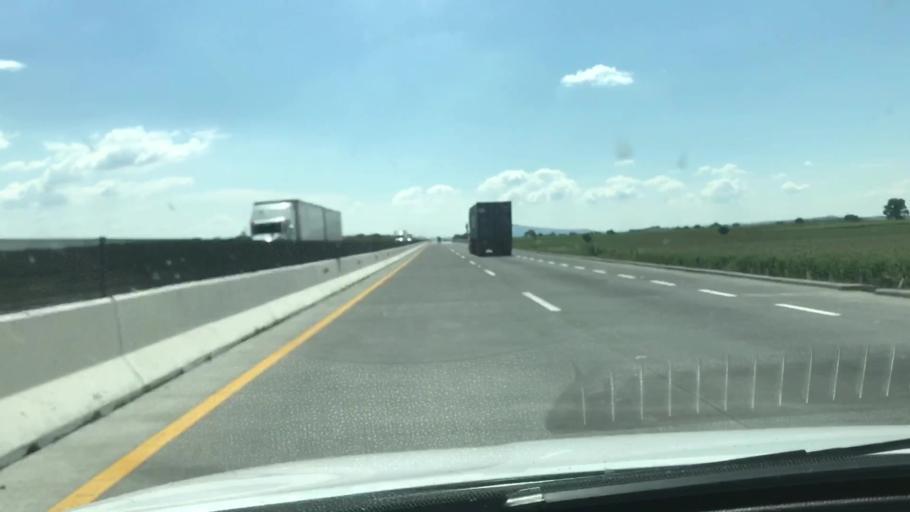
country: MX
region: Michoacan
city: La Piedad Cavadas
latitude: 20.4013
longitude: -102.0447
